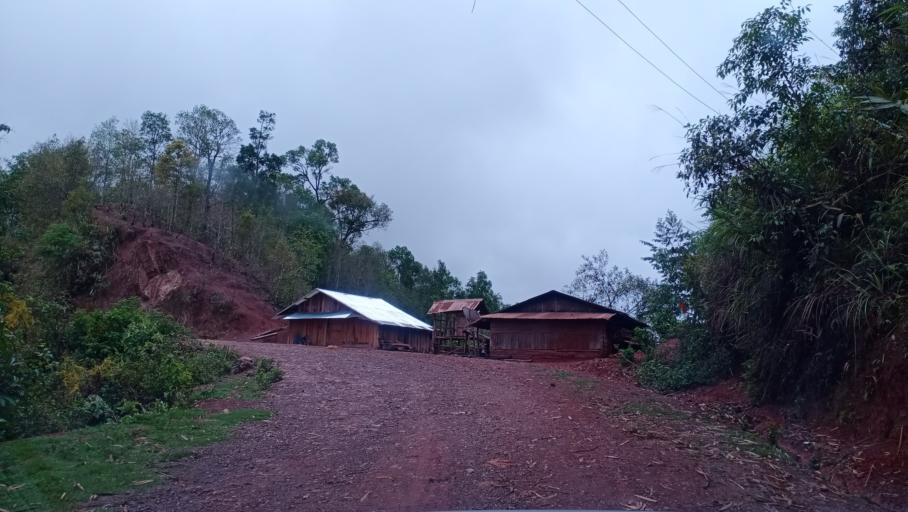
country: LA
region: Phongsali
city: Phongsali
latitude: 21.3383
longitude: 102.0806
